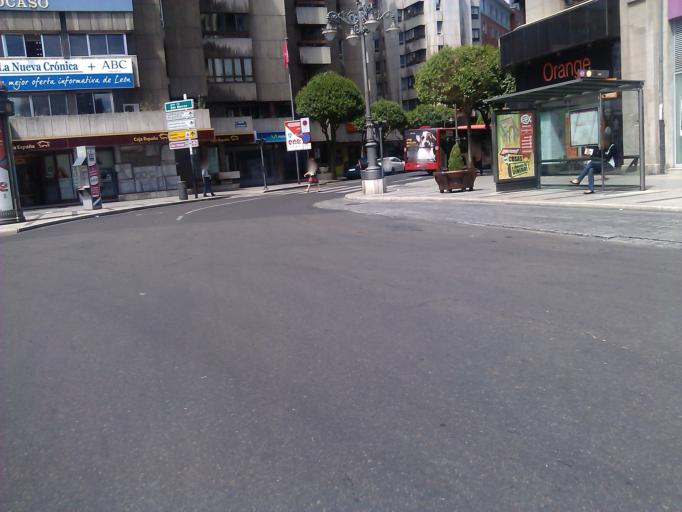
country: ES
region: Castille and Leon
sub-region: Provincia de Leon
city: Leon
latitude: 42.5982
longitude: -5.5721
